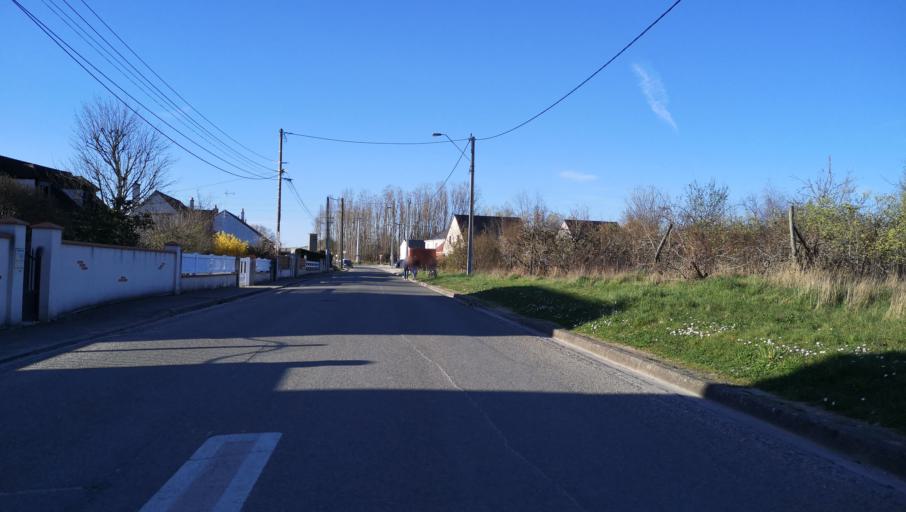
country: FR
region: Centre
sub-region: Departement du Loiret
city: Saint-Jean-de-Braye
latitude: 47.9223
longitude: 1.9719
